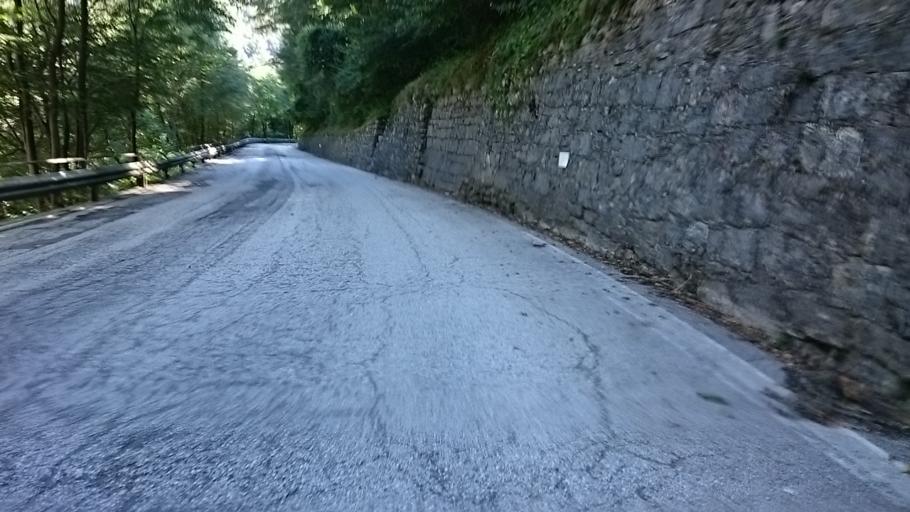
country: IT
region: Veneto
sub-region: Provincia di Belluno
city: Ospitale di Cadore
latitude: 46.3091
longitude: 12.3240
